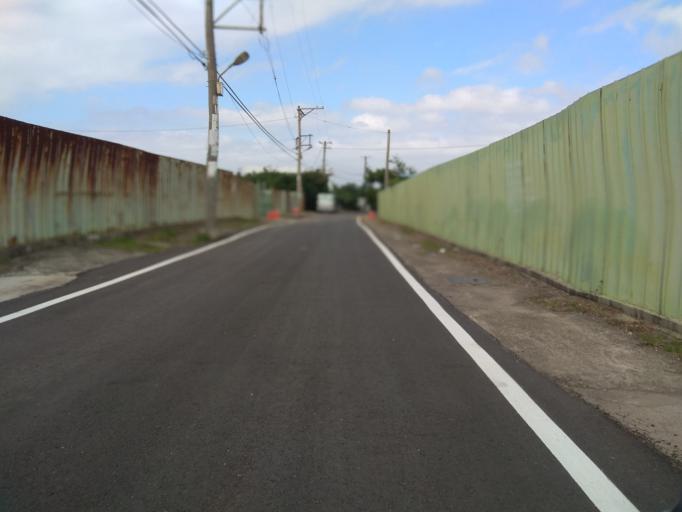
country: TW
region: Taiwan
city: Taoyuan City
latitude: 25.0606
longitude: 121.2316
